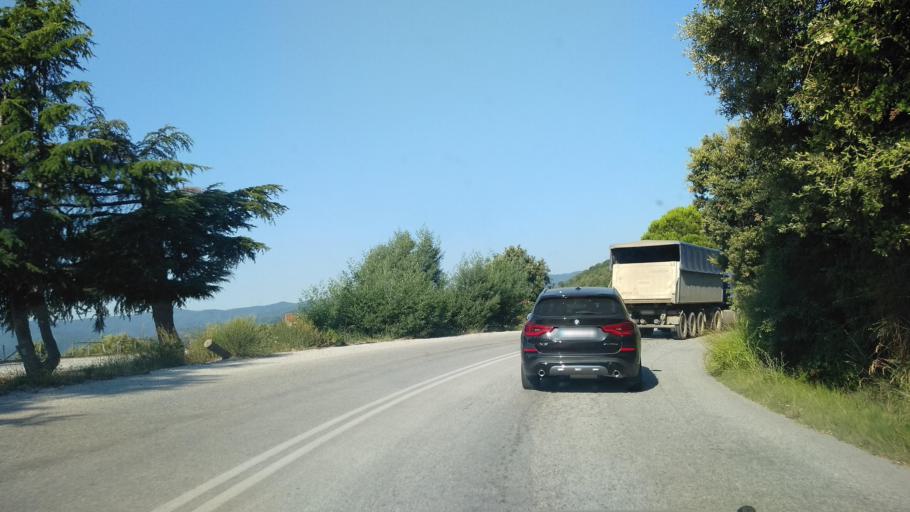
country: GR
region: Central Macedonia
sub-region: Nomos Chalkidikis
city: Stratonion
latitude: 40.5220
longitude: 23.8239
